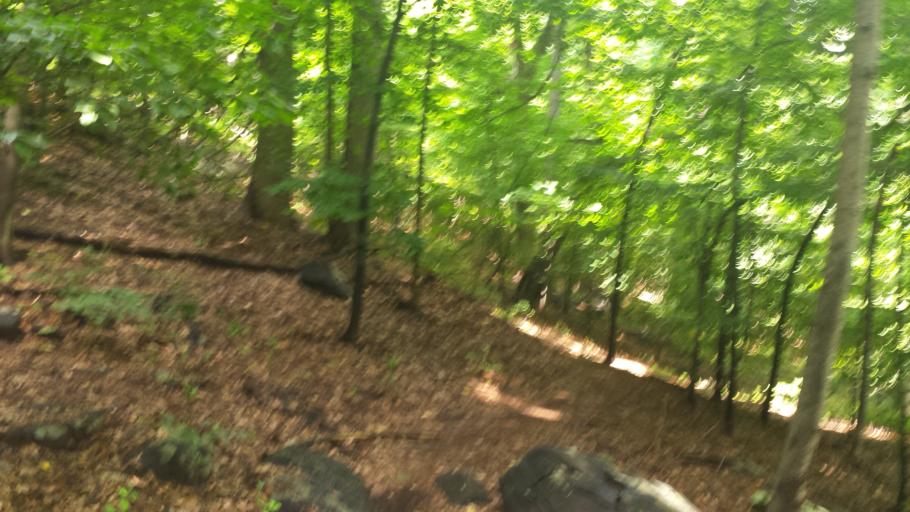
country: US
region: New York
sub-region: Westchester County
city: Hawthorne
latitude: 41.1185
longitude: -73.7956
